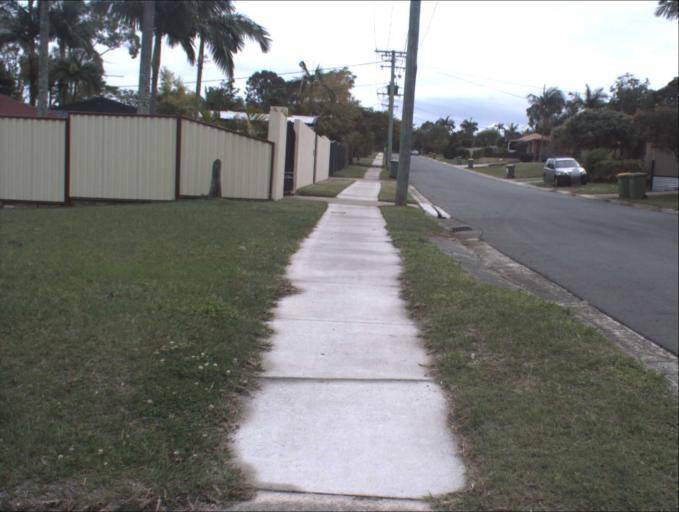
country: AU
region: Queensland
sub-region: Logan
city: Park Ridge South
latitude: -27.6882
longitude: 153.0176
